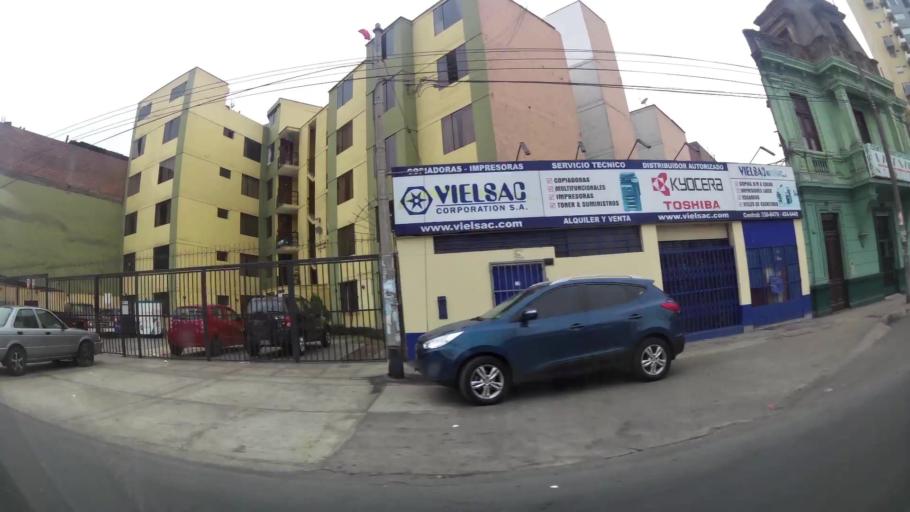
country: PE
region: Lima
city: Lima
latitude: -12.0654
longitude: -77.0448
